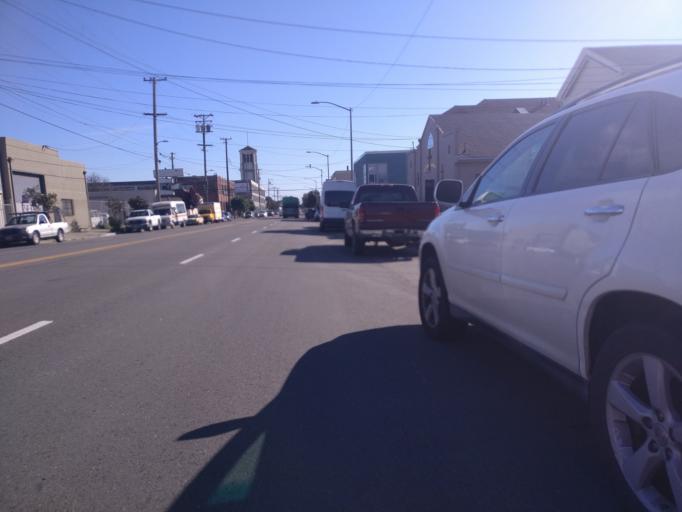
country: US
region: California
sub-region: Alameda County
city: Emeryville
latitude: 37.8182
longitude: -122.2831
